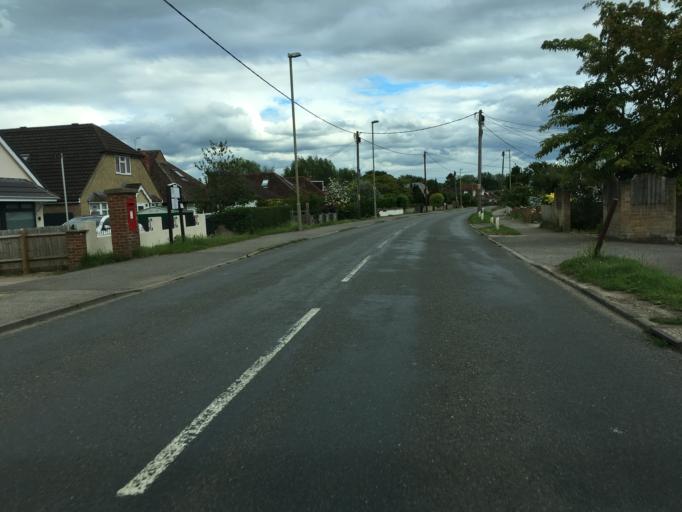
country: GB
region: England
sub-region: Oxfordshire
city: Boars Hill
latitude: 51.6968
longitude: -1.2997
